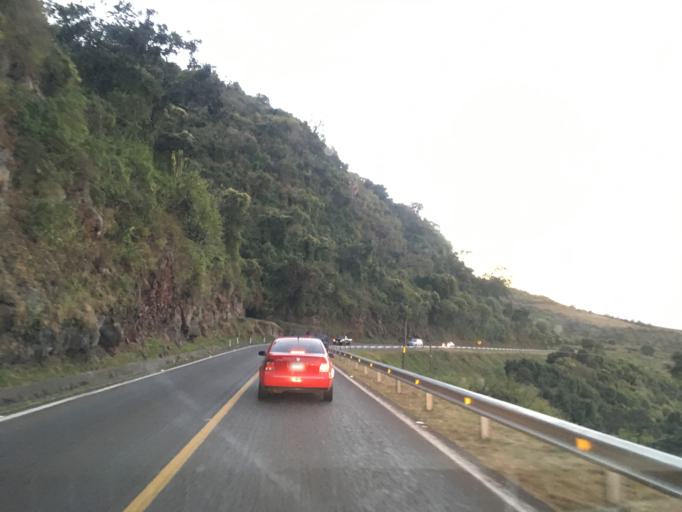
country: MX
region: Michoacan
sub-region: Zinapecuaro
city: Santa Clara del Tule
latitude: 19.8109
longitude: -100.8174
